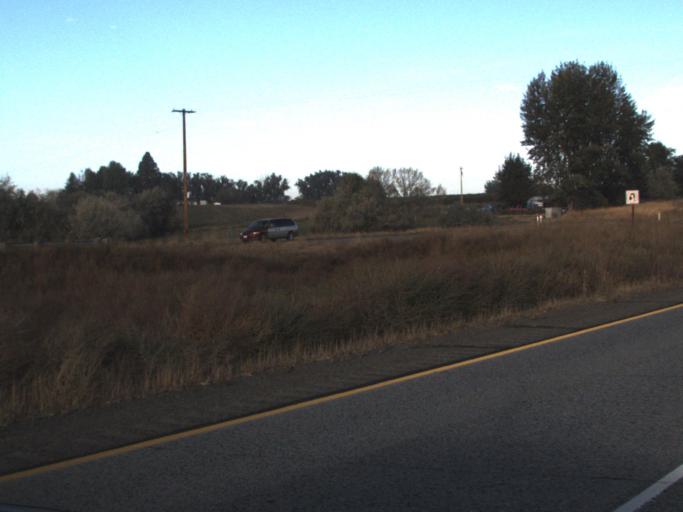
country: US
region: Washington
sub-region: Yakima County
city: Sunnyside
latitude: 46.2933
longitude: -119.9542
